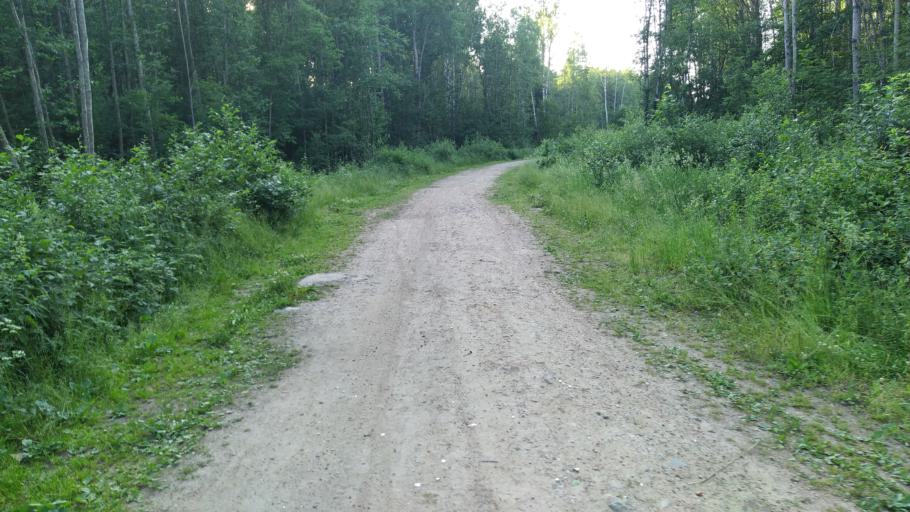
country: RU
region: Leningrad
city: Toksovo
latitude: 60.1095
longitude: 30.5239
